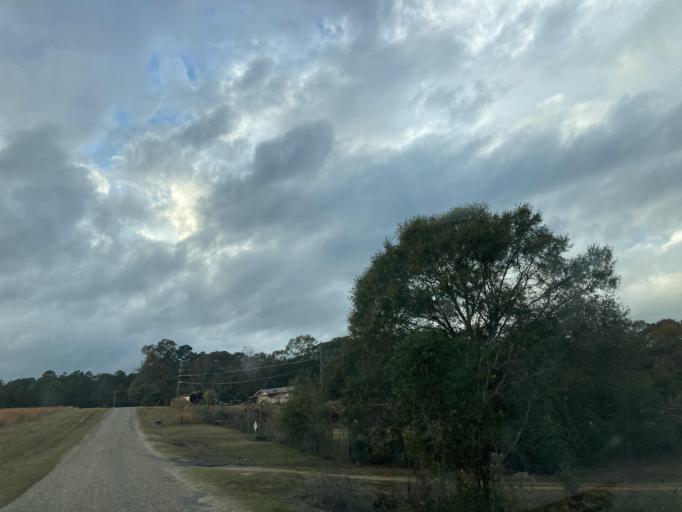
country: US
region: Mississippi
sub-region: Marion County
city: Columbia
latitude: 31.1969
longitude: -89.6300
